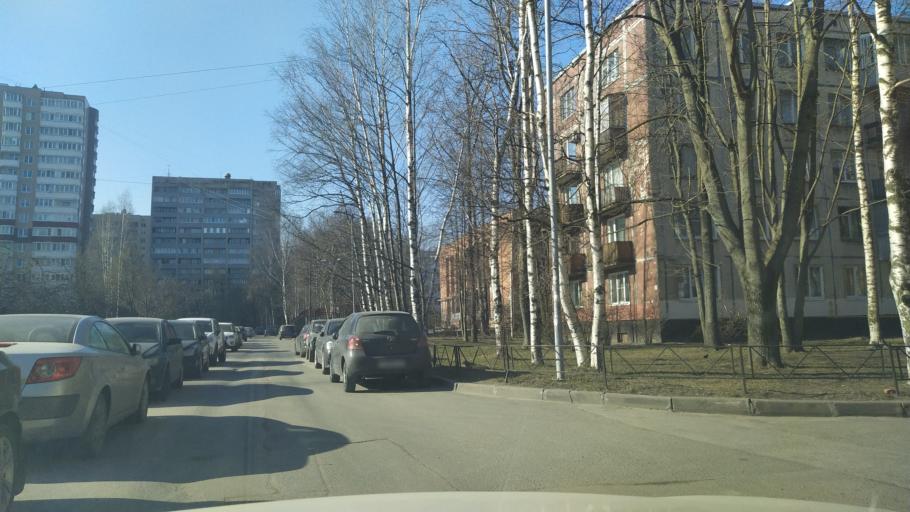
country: RU
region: Leningrad
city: Akademicheskoe
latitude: 60.0184
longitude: 30.3967
